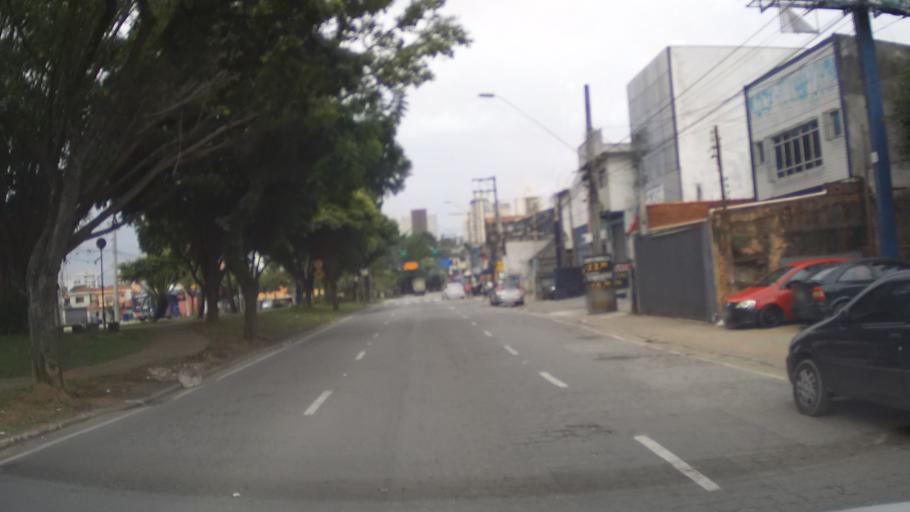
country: BR
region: Sao Paulo
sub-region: Guarulhos
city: Guarulhos
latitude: -23.4589
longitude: -46.5702
